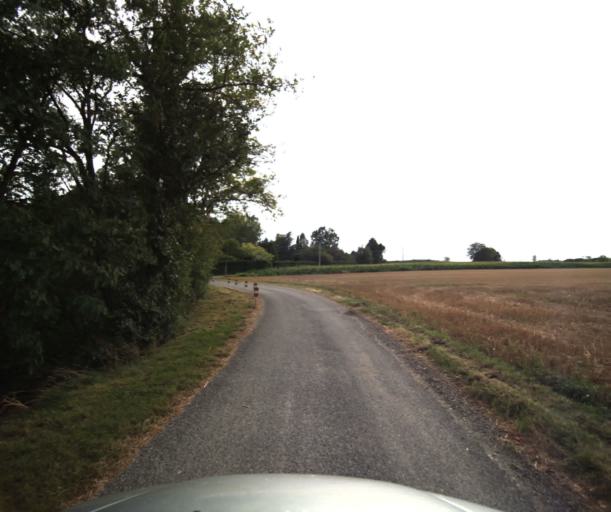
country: FR
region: Midi-Pyrenees
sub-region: Departement de la Haute-Garonne
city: Le Fauga
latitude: 43.4256
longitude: 1.3151
